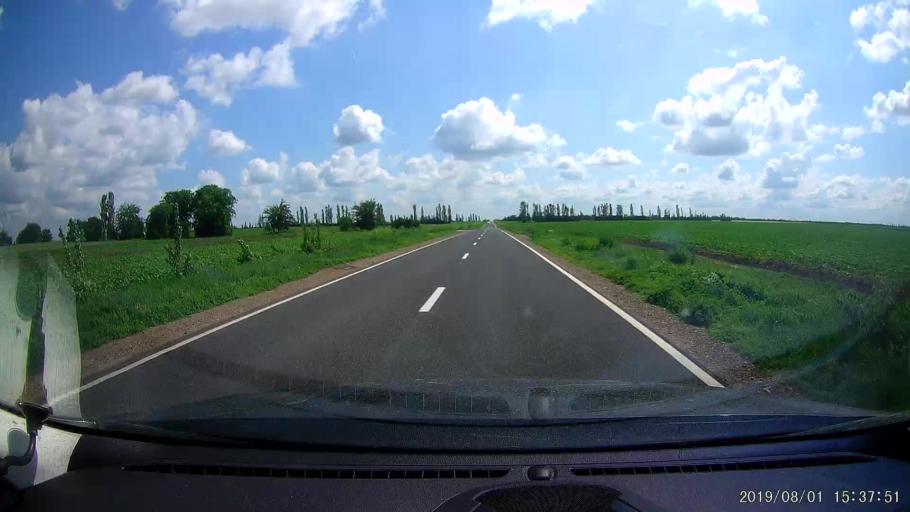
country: RO
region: Braila
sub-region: Comuna Insuratei
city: Insuratei
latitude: 44.8954
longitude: 27.5845
